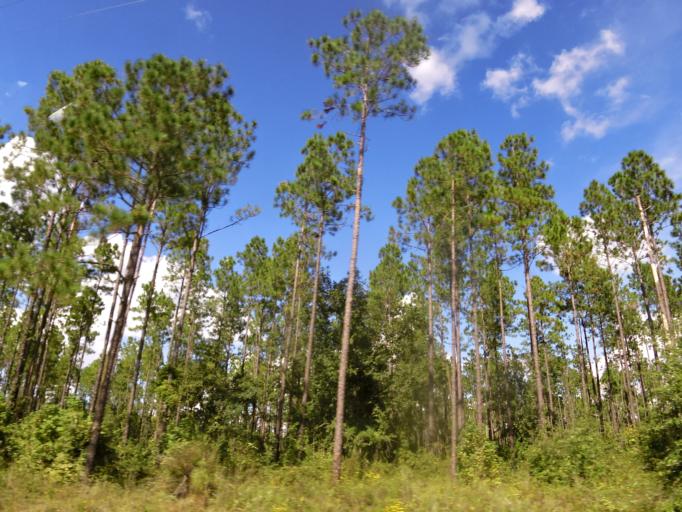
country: US
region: Georgia
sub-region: Echols County
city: Statenville
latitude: 30.7669
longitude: -83.1320
